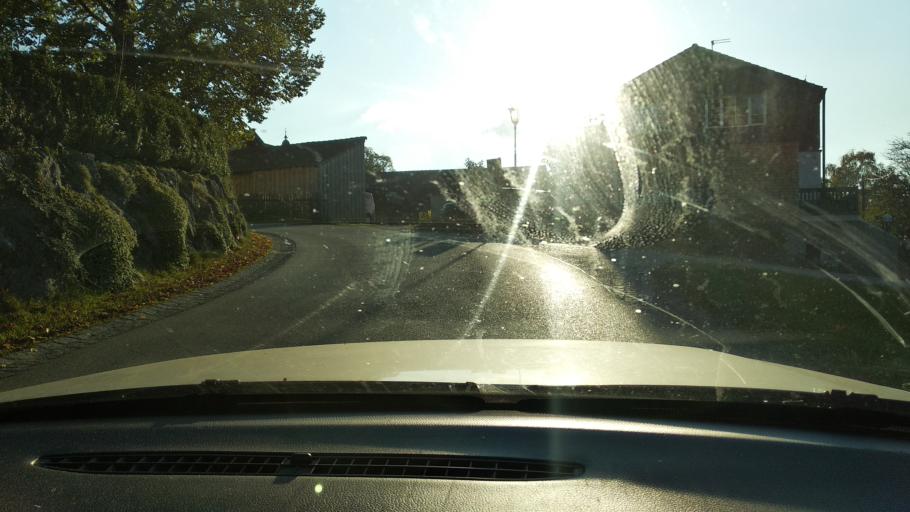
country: DE
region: Bavaria
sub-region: Upper Bavaria
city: Glonn
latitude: 47.9721
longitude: 11.8373
